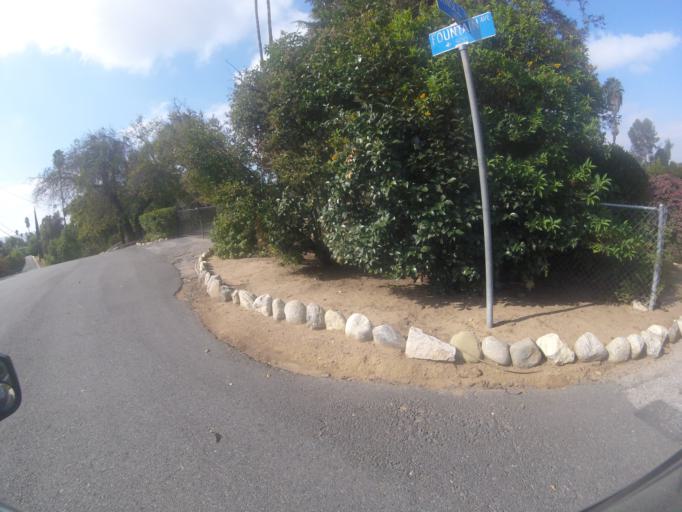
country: US
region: California
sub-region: San Bernardino County
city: Redlands
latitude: 34.0342
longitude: -117.1710
